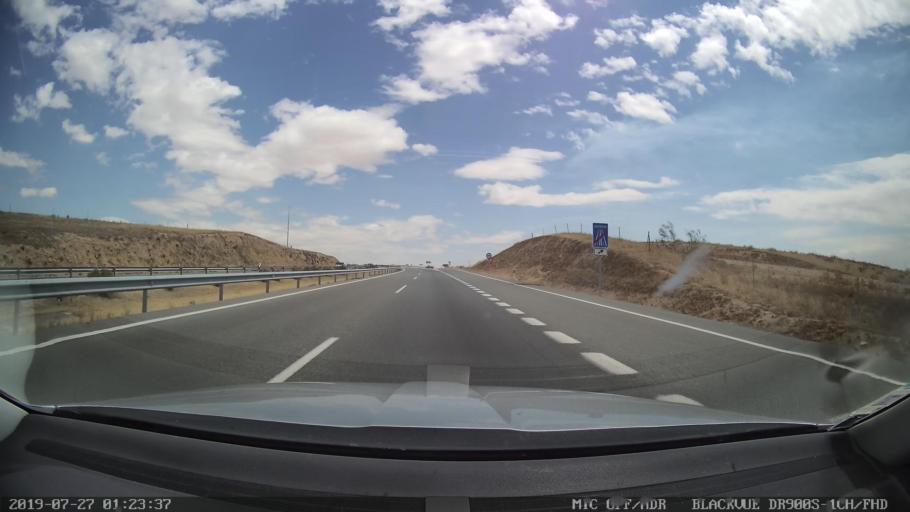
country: ES
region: Castille-La Mancha
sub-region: Province of Toledo
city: Santa Cruz del Retamar
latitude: 40.1255
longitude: -4.2285
